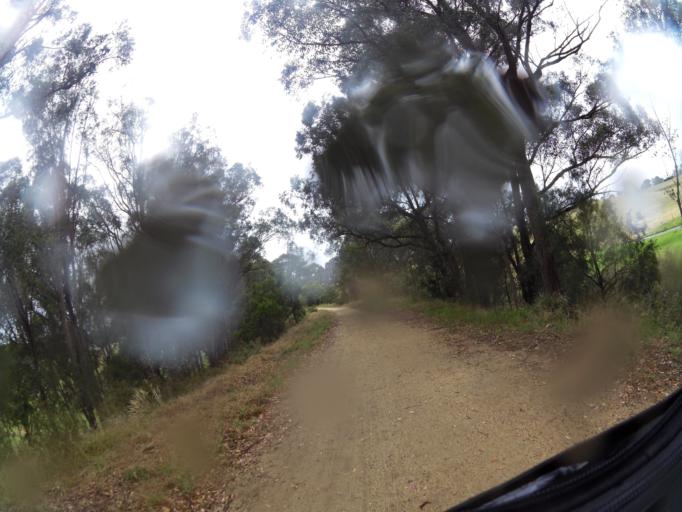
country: AU
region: Victoria
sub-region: East Gippsland
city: Lakes Entrance
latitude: -37.7610
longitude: 147.8173
